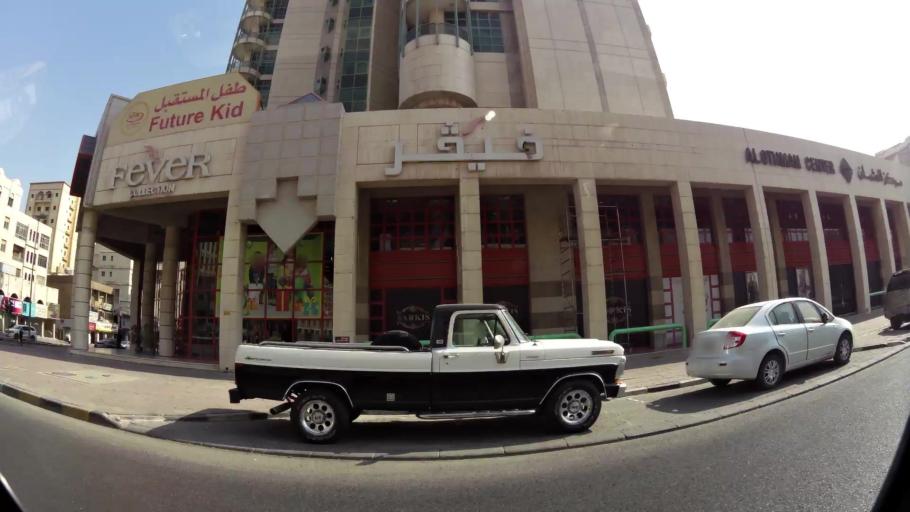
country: KW
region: Muhafazat Hawalli
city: Hawalli
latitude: 29.3429
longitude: 48.0132
